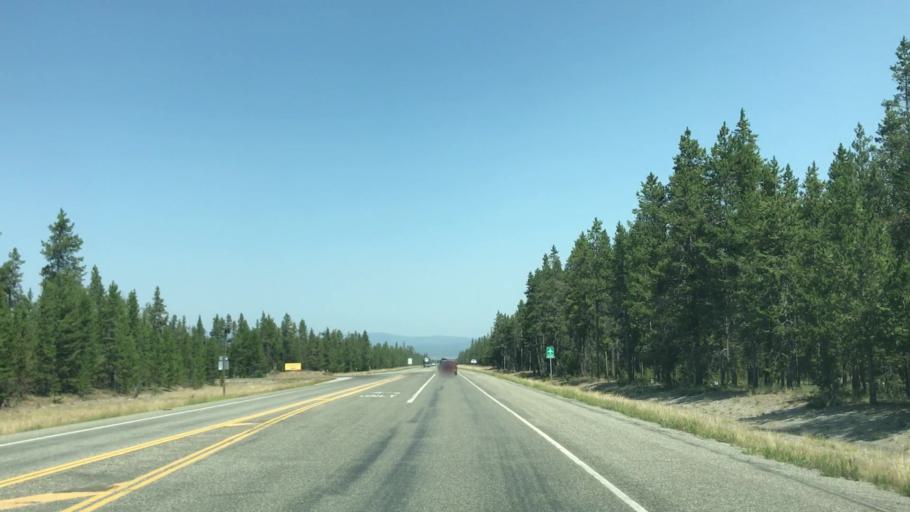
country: US
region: Montana
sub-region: Gallatin County
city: West Yellowstone
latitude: 44.6859
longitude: -111.1011
